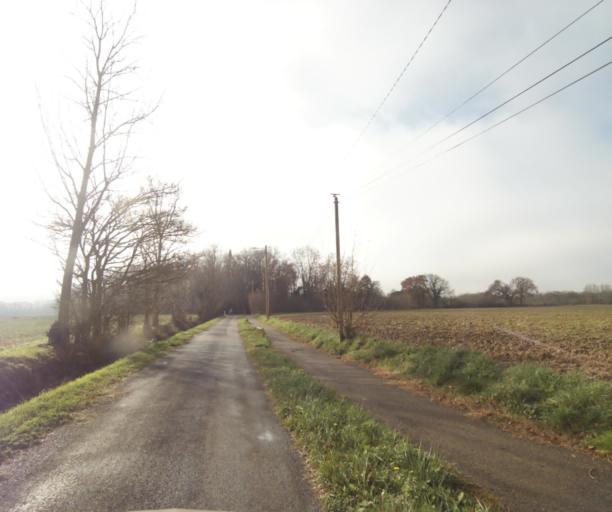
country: FR
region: Midi-Pyrenees
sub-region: Departement de la Haute-Garonne
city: Villemur-sur-Tarn
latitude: 43.8556
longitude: 1.4962
